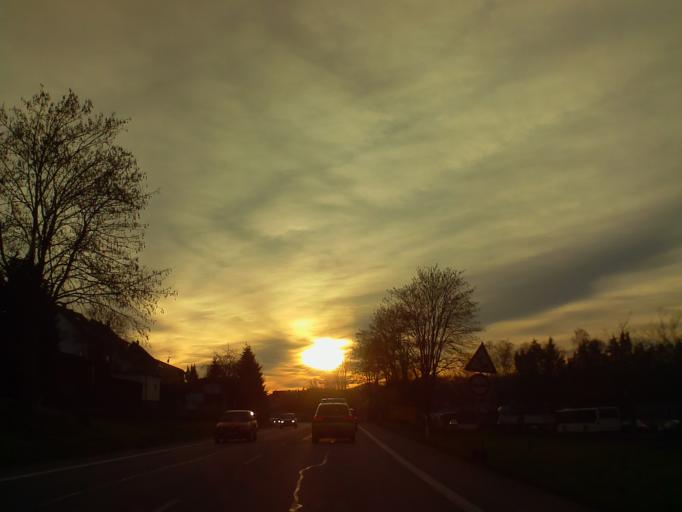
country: DE
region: Hesse
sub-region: Regierungsbezirk Darmstadt
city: Morlenbach
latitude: 49.6018
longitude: 8.7434
